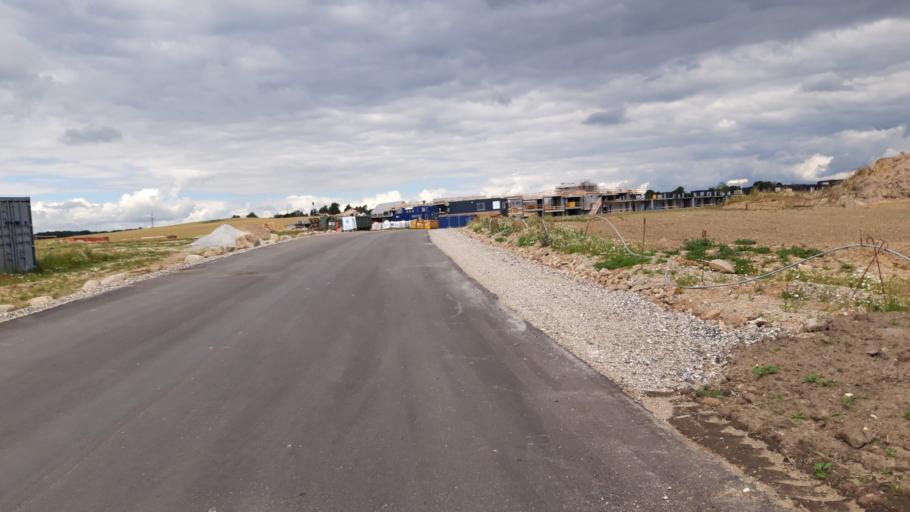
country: DK
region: Central Jutland
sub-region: Arhus Kommune
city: Lystrup
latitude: 56.2313
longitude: 10.2069
